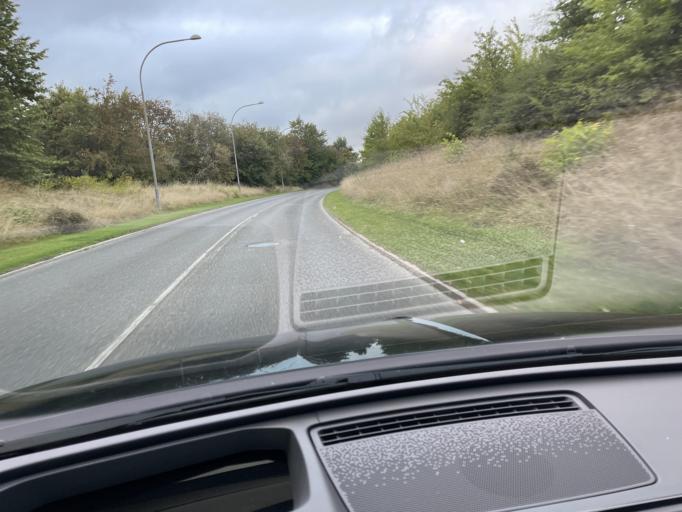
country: DK
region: Zealand
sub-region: Solrod Kommune
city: Havdrup
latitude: 55.5390
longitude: 12.1212
